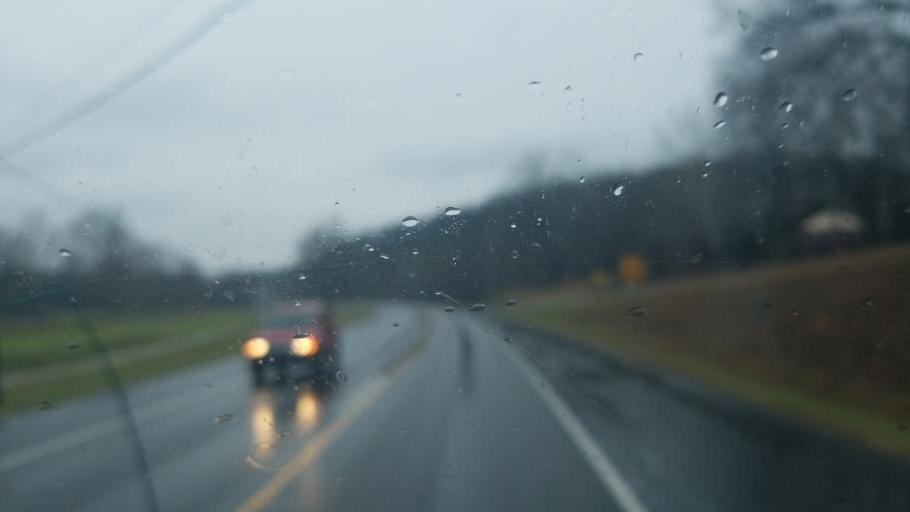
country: US
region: Indiana
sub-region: Brown County
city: Nashville
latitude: 39.1957
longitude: -86.2048
